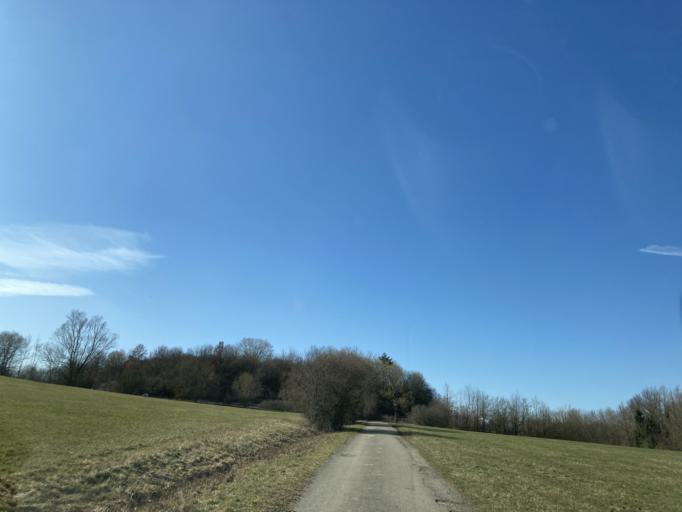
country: DE
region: Baden-Wuerttemberg
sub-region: Tuebingen Region
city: Bodelshausen
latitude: 48.3855
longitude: 8.9989
